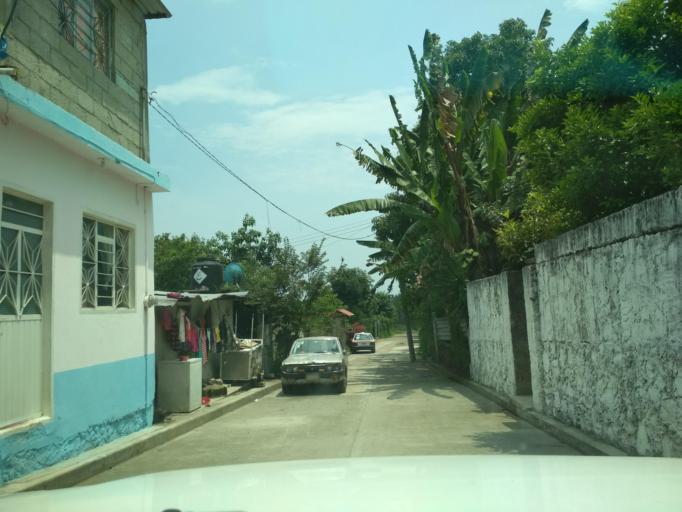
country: MX
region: Veracruz
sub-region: Mariano Escobedo
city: Mariano Escobedo
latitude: 18.9088
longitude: -97.1280
